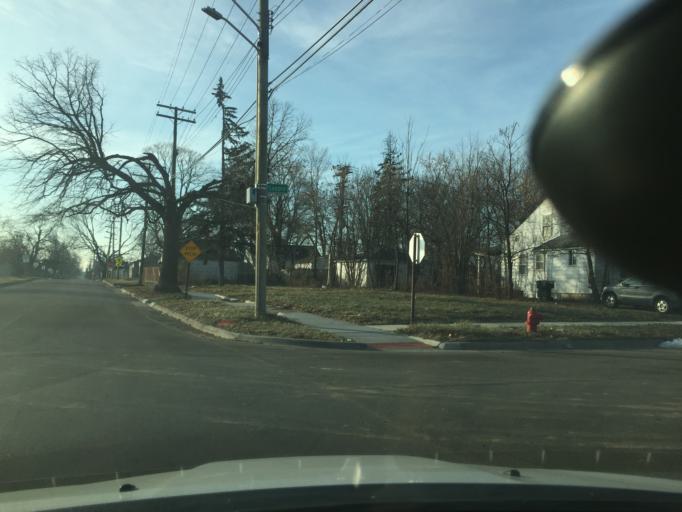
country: US
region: Michigan
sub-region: Macomb County
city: Eastpointe
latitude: 42.4373
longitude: -82.9631
